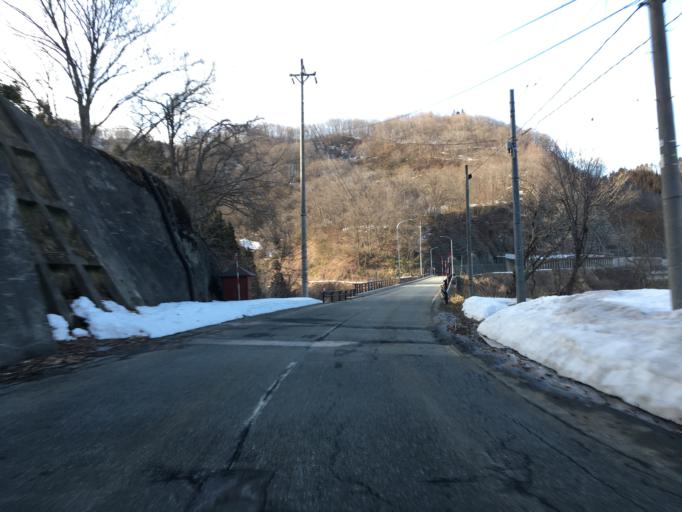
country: JP
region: Yamagata
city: Nagai
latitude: 37.9613
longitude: 139.9133
